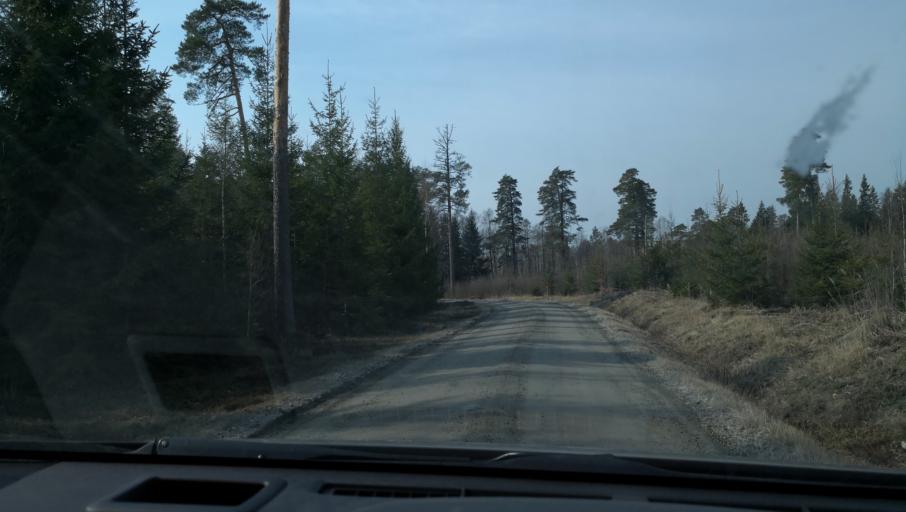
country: SE
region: OErebro
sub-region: Lindesbergs Kommun
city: Frovi
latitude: 59.3639
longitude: 15.4320
